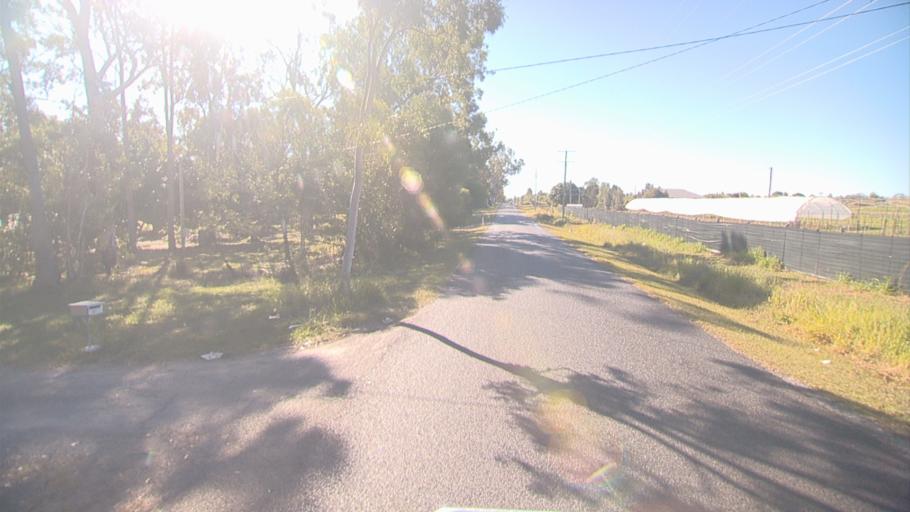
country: AU
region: Queensland
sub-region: Logan
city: Logan Reserve
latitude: -27.7254
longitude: 153.0732
